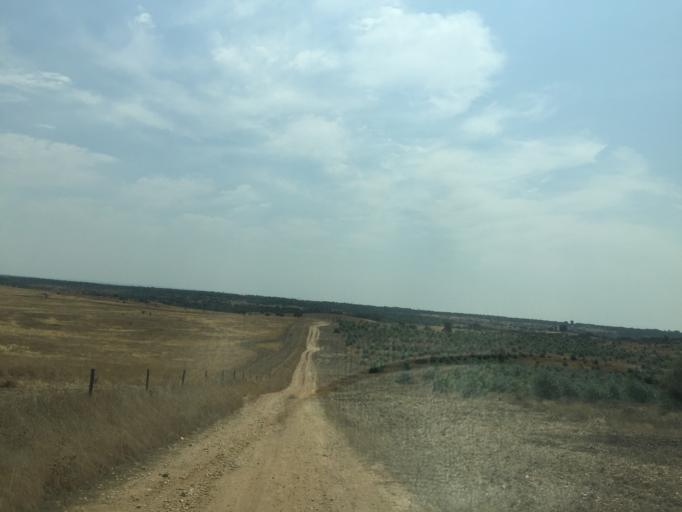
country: PT
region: Setubal
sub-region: Grandola
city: Grandola
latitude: 38.0483
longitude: -8.4537
